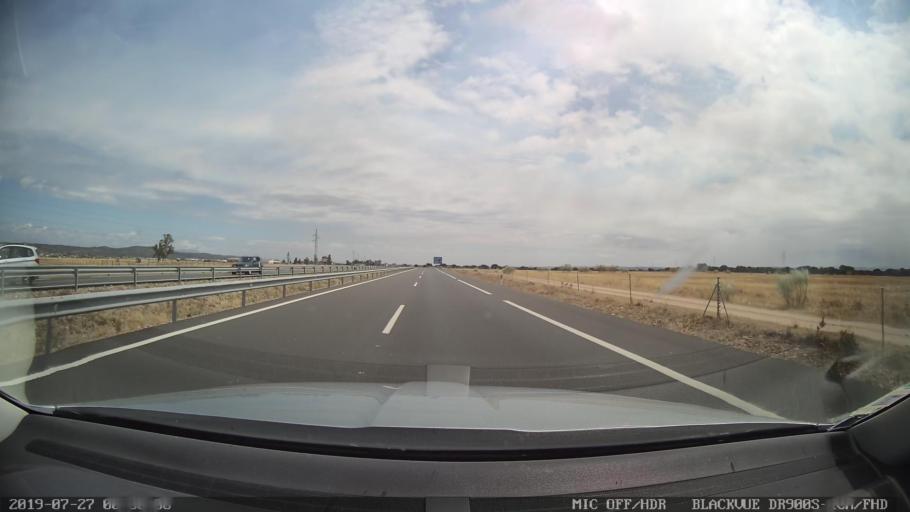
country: ES
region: Castille-La Mancha
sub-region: Province of Toledo
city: Velada
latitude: 39.9384
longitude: -4.9698
